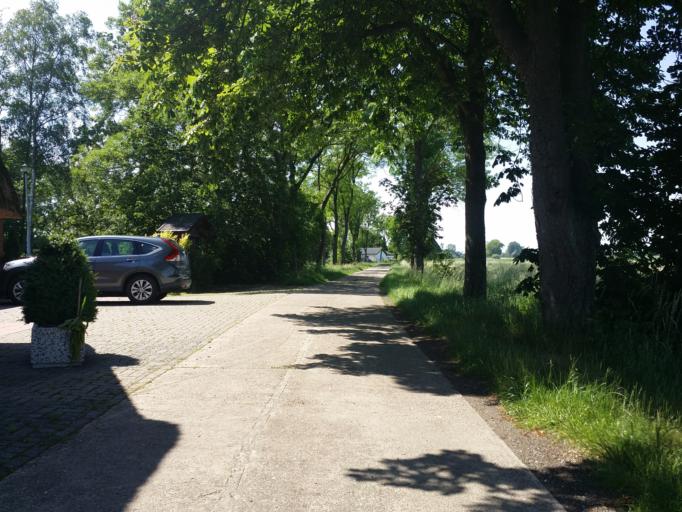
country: DE
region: Lower Saxony
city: Neuenkirchen
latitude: 53.1596
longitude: 8.5339
